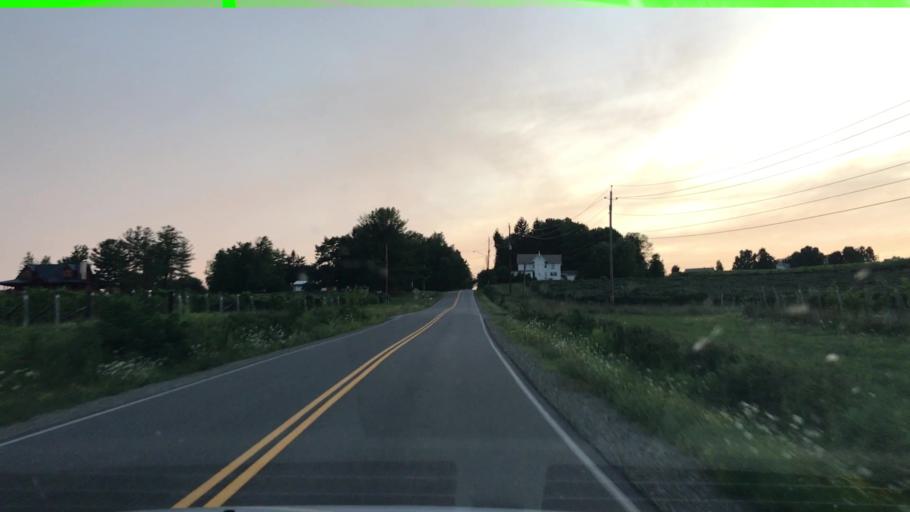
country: US
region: New York
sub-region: Steuben County
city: Sylvan Beach
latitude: 42.5286
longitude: -77.1586
